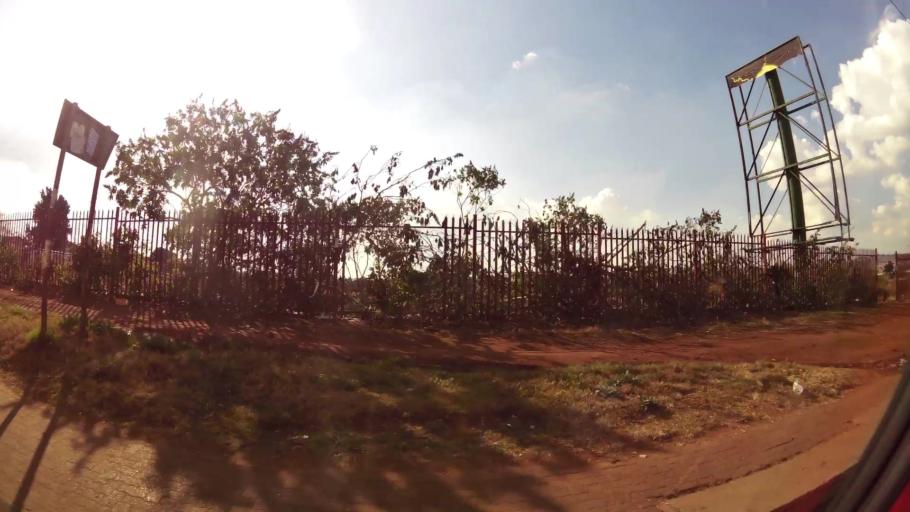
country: ZA
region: Gauteng
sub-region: City of Johannesburg Metropolitan Municipality
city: Roodepoort
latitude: -26.2149
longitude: 27.8687
